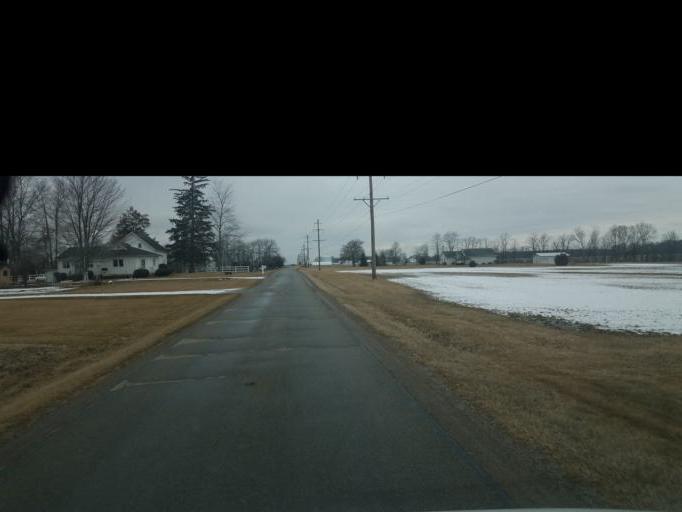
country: US
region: Ohio
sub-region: Defiance County
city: Hicksville
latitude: 41.3536
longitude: -84.7548
